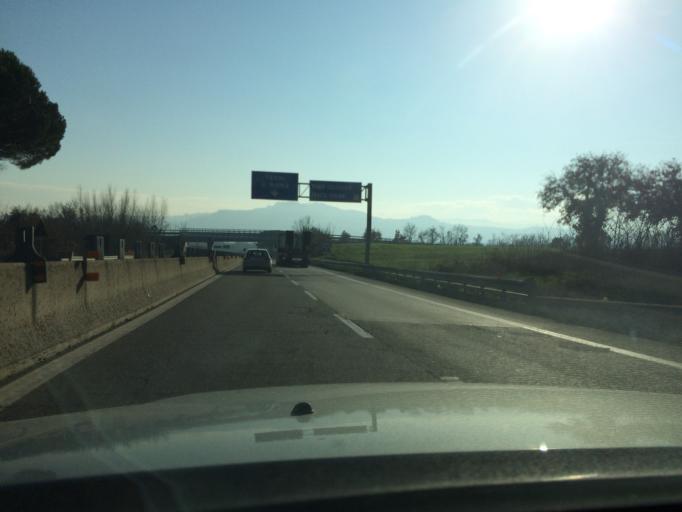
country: IT
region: Umbria
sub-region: Provincia di Perugia
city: Ponterio-Pian di Porto
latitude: 42.8224
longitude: 12.3993
